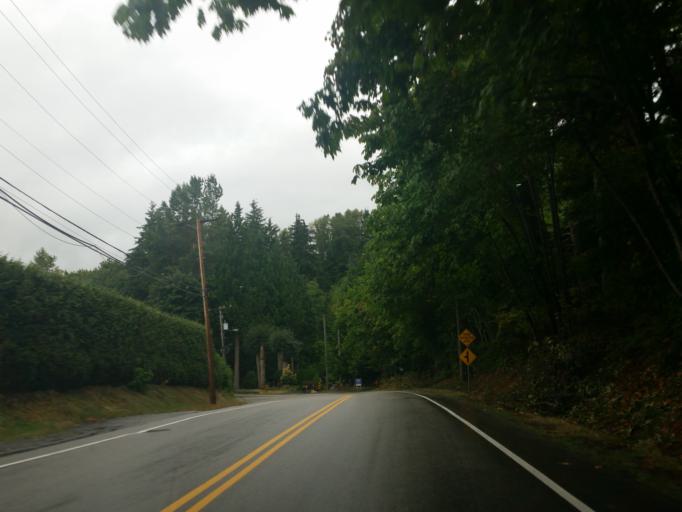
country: CA
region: British Columbia
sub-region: Greater Vancouver Regional District
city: Anmore
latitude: 49.3017
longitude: -122.8696
